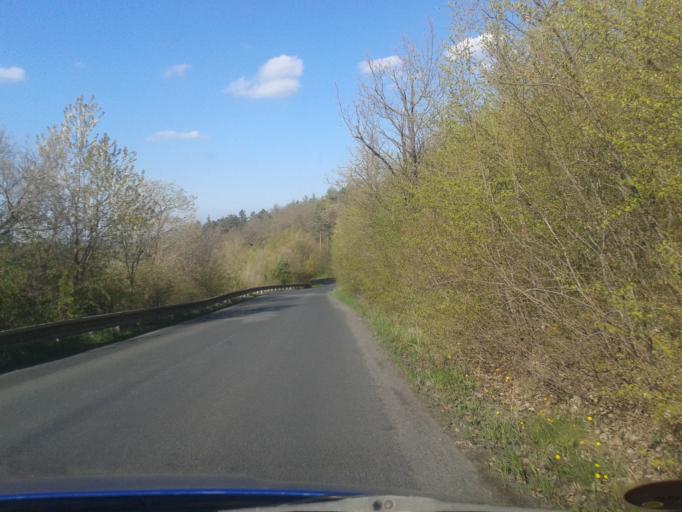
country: CZ
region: Central Bohemia
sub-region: Okres Beroun
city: Beroun
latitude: 49.9109
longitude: 14.0740
